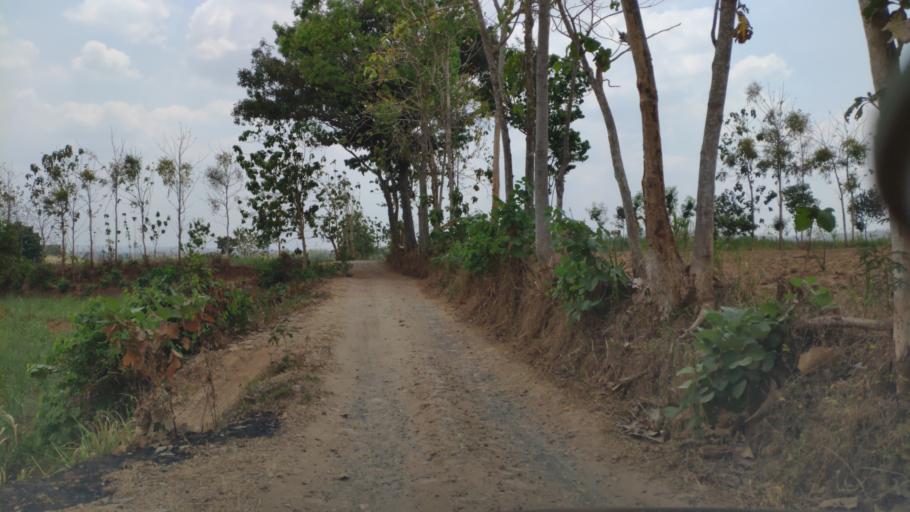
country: ID
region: Central Java
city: Kalinanas
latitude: -6.8648
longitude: 111.2443
